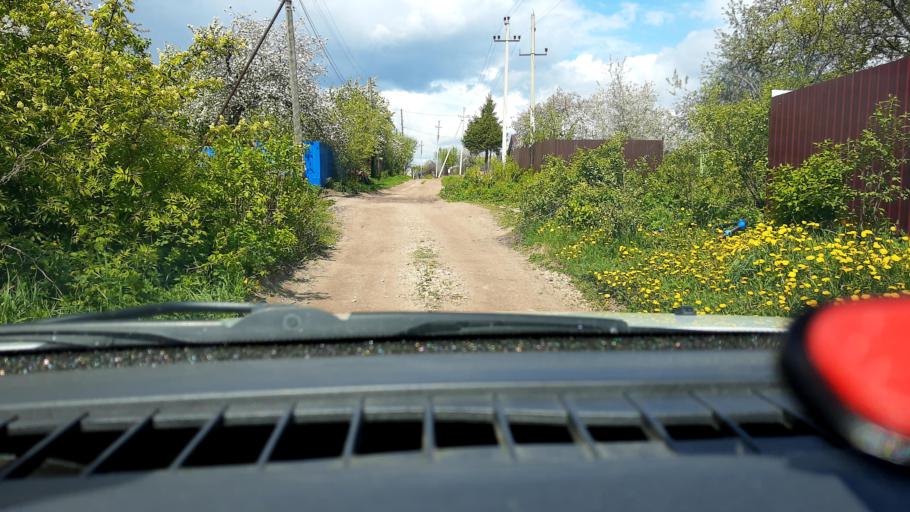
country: RU
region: Nizjnij Novgorod
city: Afonino
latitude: 56.2748
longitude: 44.0797
